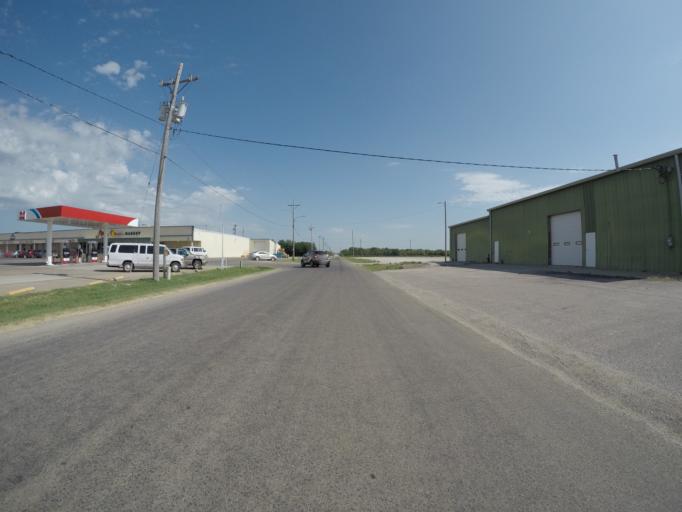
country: US
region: Kansas
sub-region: Clay County
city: Clay Center
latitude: 39.3798
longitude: -97.1464
